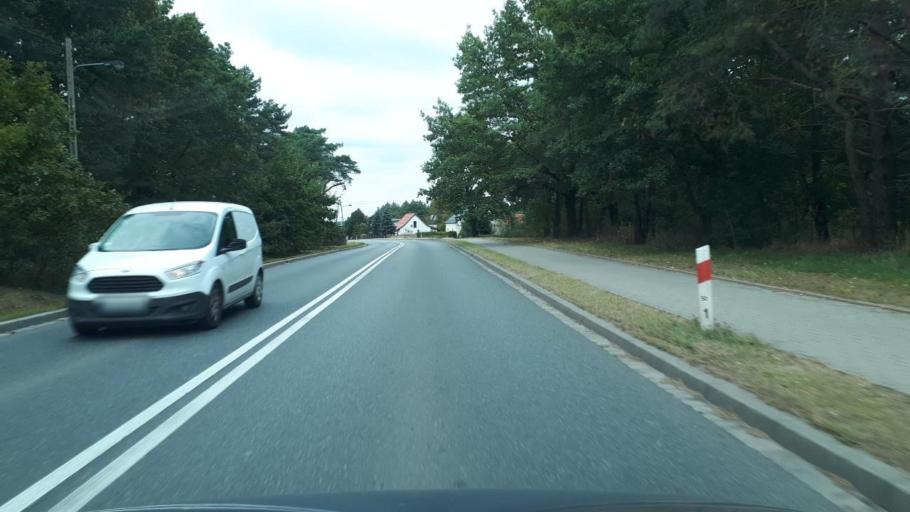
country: PL
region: Opole Voivodeship
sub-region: Powiat oleski
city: Olesno
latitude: 50.8913
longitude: 18.3995
